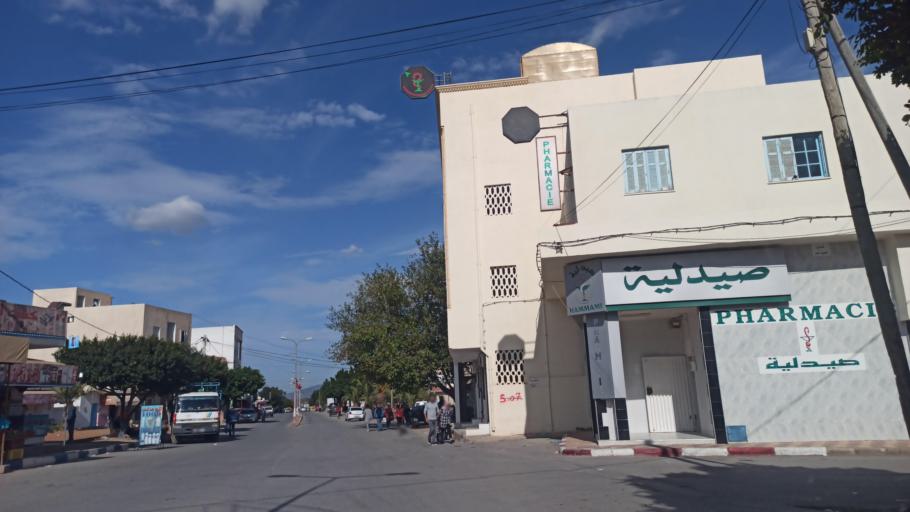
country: TN
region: Zaghwan
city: Zaghouan
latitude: 36.3518
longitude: 10.2084
